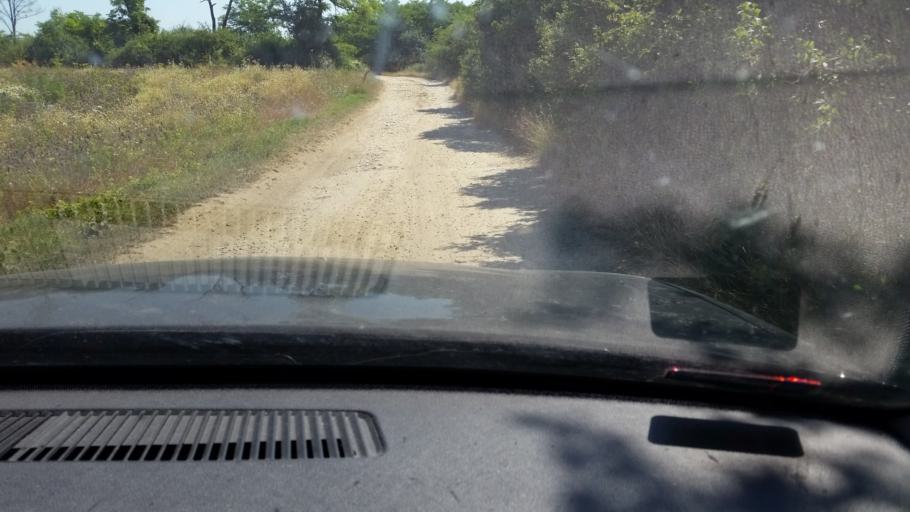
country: HU
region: Fejer
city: Many
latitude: 47.5447
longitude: 18.6119
